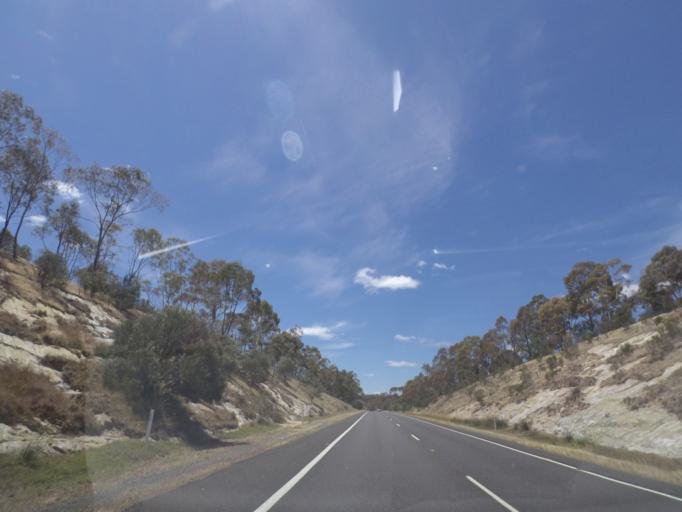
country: AU
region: Victoria
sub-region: Mount Alexander
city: Castlemaine
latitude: -37.1633
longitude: 144.1540
